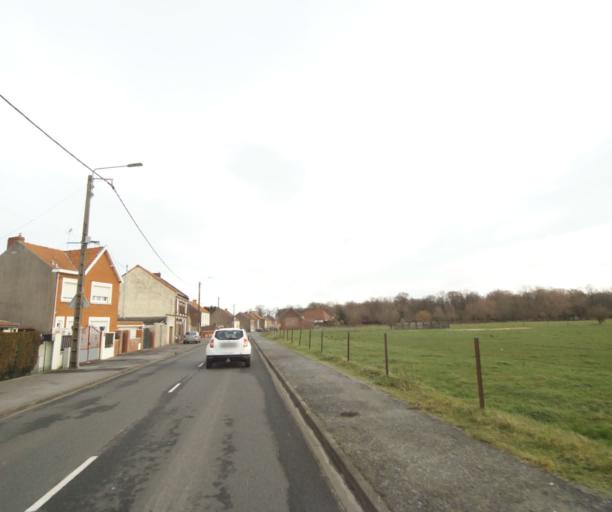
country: FR
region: Nord-Pas-de-Calais
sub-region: Departement du Nord
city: Vieux-Conde
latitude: 50.4829
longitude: 3.5805
